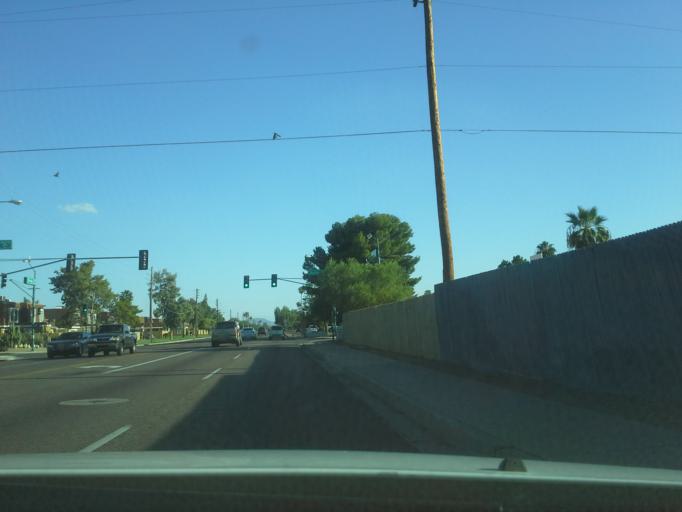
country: US
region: Arizona
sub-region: Maricopa County
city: Glendale
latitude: 33.5609
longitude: -112.1343
